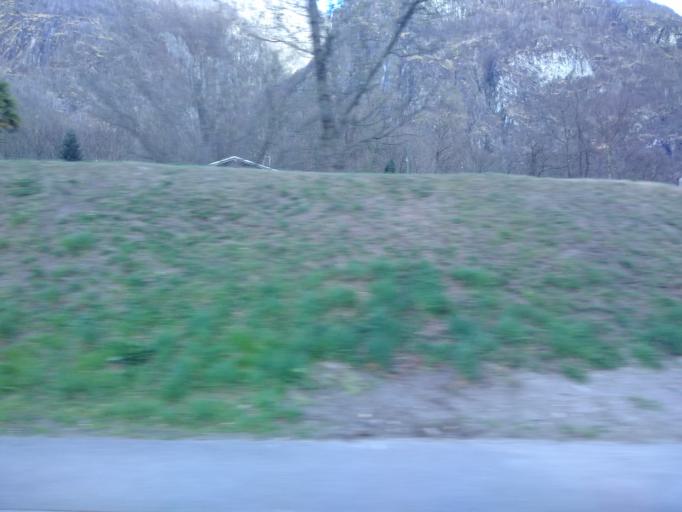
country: CH
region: Ticino
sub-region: Locarno District
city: Verscio
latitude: 46.2038
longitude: 8.7431
